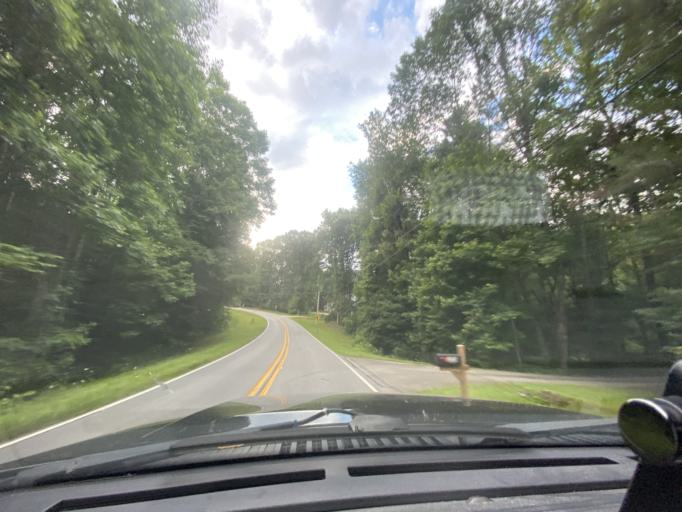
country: US
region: Georgia
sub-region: Fayette County
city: Peachtree City
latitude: 33.4194
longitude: -84.6650
